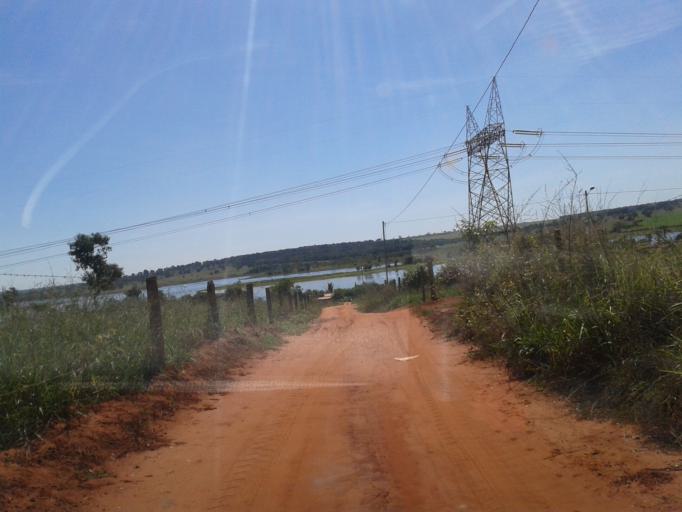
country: BR
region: Minas Gerais
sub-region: Santa Vitoria
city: Santa Vitoria
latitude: -19.0089
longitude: -50.3264
